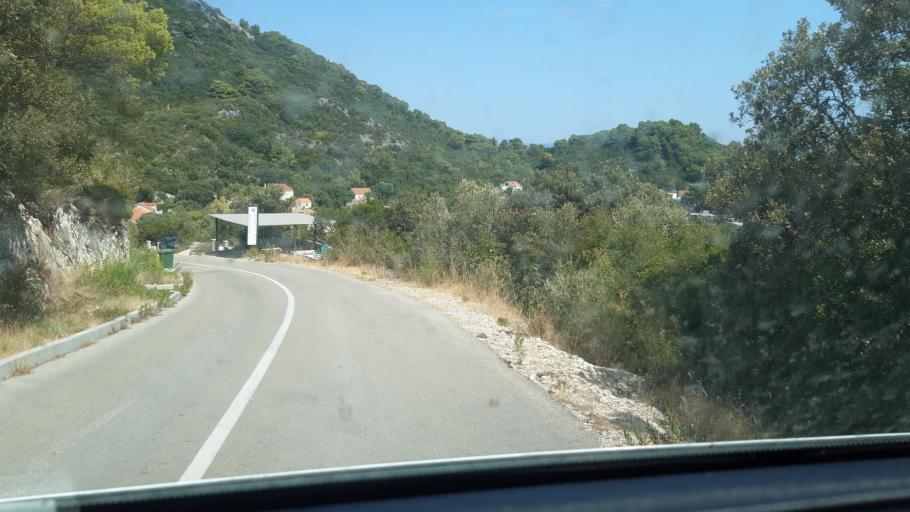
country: HR
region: Dubrovacko-Neretvanska
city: Ston
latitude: 42.7246
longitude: 17.6686
